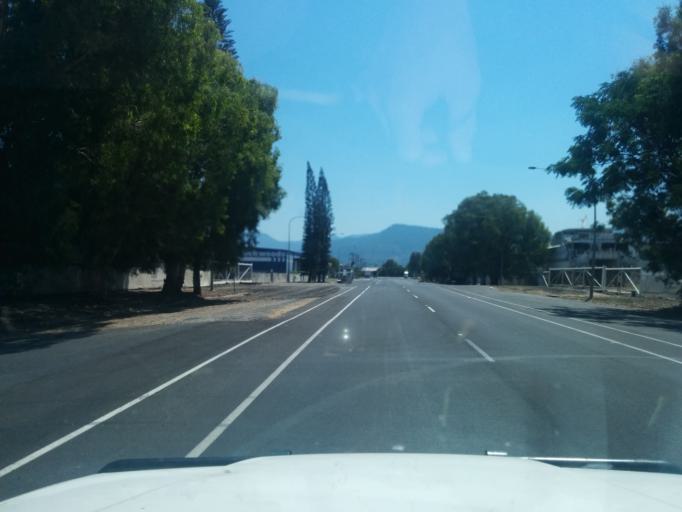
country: AU
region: Queensland
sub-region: Cairns
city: Cairns
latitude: -16.9407
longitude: 145.7737
